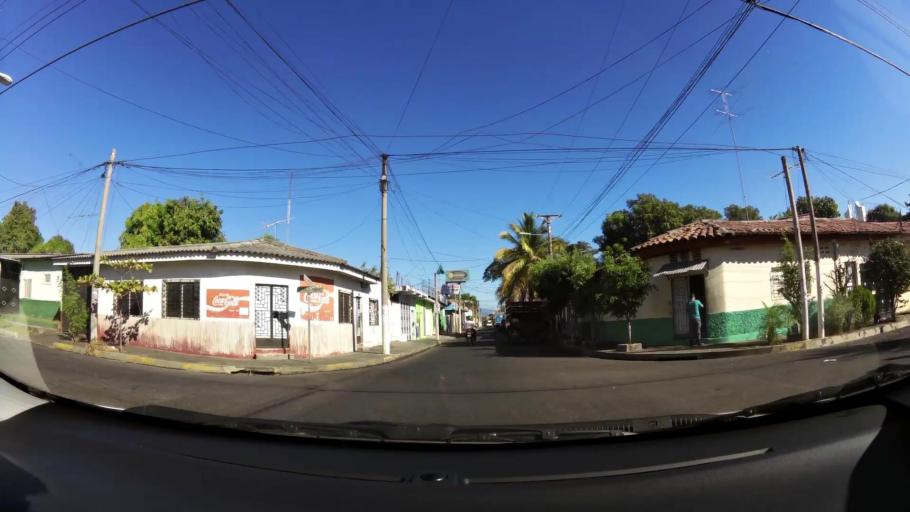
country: SV
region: San Miguel
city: San Miguel
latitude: 13.4692
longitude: -88.1770
